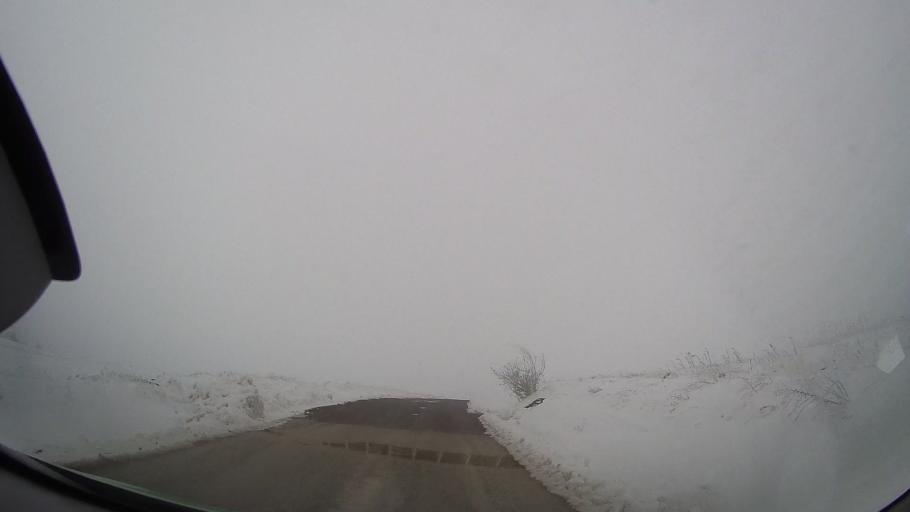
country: RO
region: Iasi
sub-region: Comuna Dagata
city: Dagata
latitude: 46.9062
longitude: 27.1966
